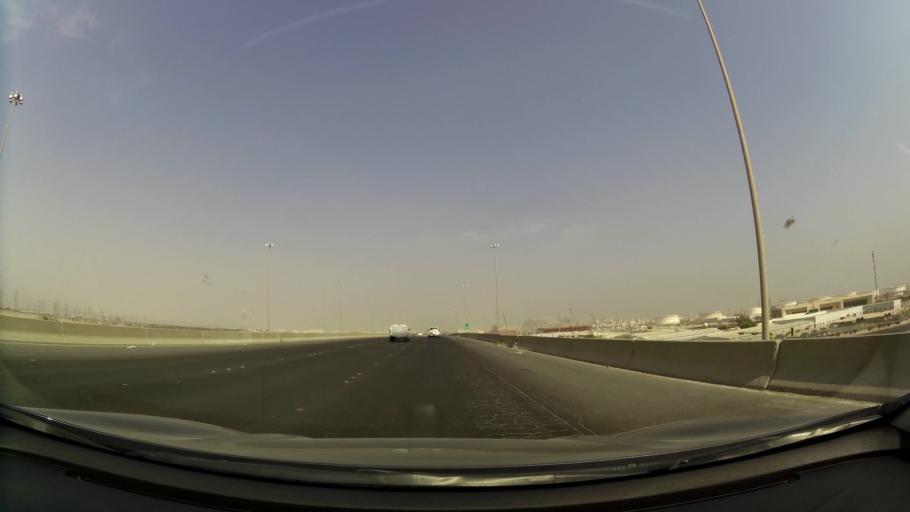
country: KW
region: Al Ahmadi
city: Al Ahmadi
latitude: 29.0615
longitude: 48.1089
